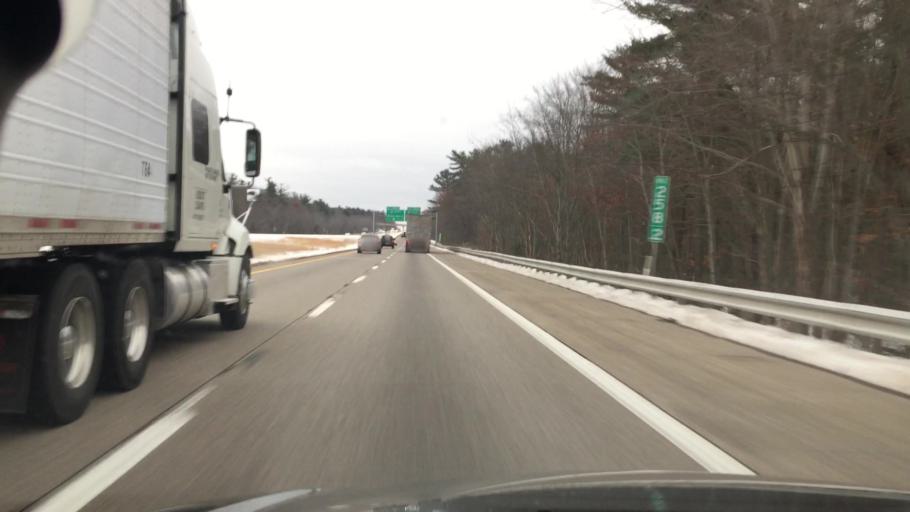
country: US
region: Pennsylvania
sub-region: Luzerne County
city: Conyngham
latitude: 41.0391
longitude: -76.0417
